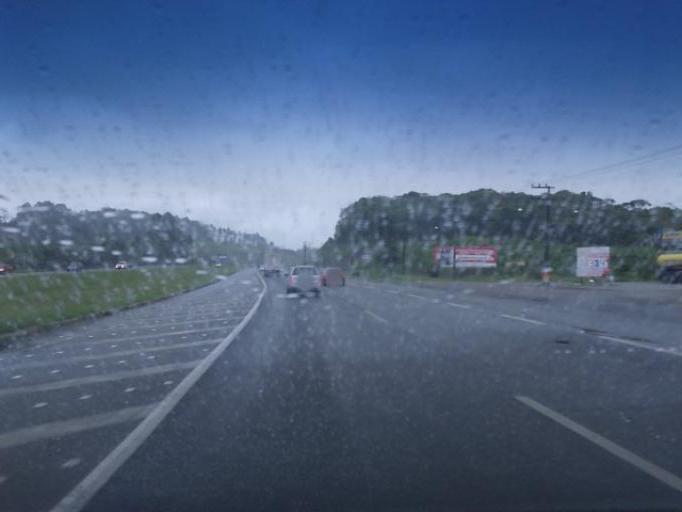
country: BR
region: Santa Catarina
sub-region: Penha
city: Penha
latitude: -26.7329
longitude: -48.7003
